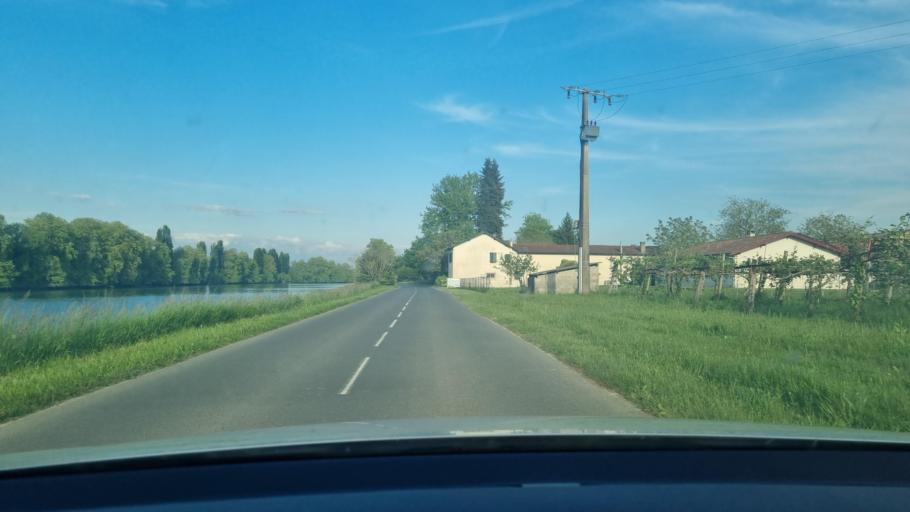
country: FR
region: Aquitaine
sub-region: Departement des Landes
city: Peyrehorade
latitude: 43.5458
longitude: -1.1790
